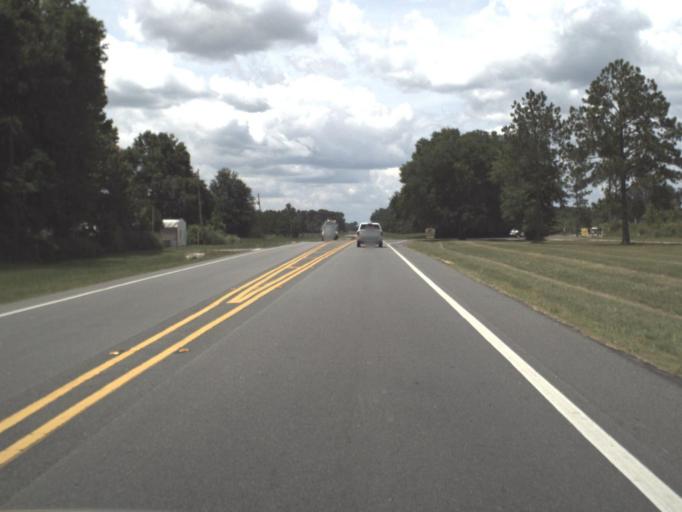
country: US
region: Florida
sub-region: Alachua County
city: Newberry
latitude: 29.6676
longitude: -82.6069
